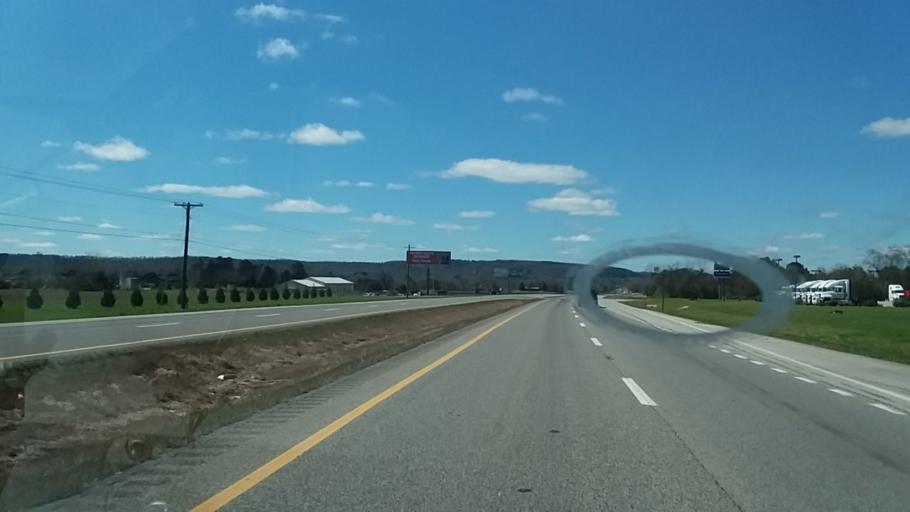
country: US
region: Alabama
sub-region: Colbert County
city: Tuscumbia
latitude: 34.7095
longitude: -87.7385
